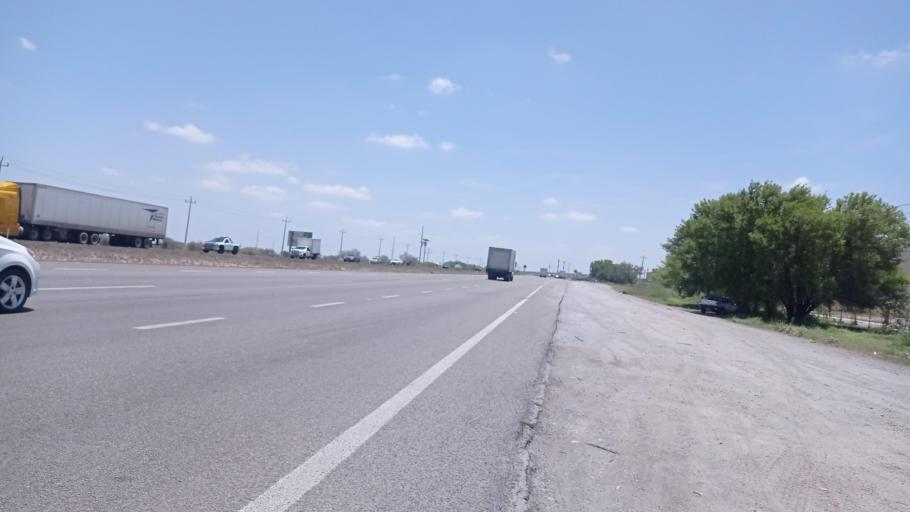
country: MX
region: Nuevo Leon
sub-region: General Zuazua
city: Villas de Alcala
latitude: 25.8930
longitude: -100.2227
